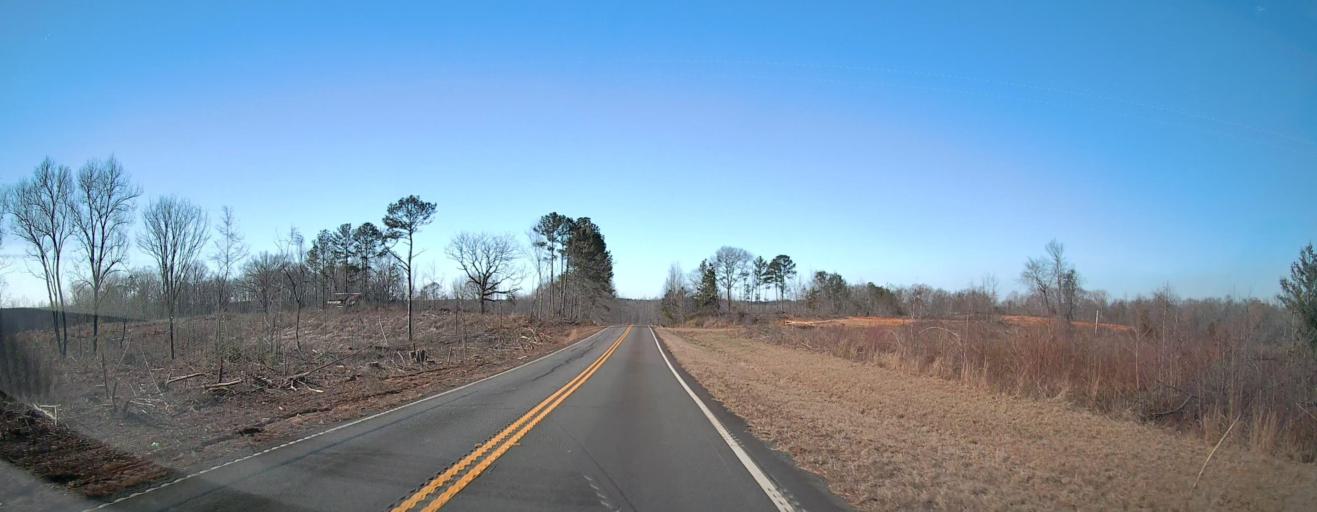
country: US
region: Georgia
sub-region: Talbot County
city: Talbotton
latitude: 32.6659
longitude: -84.4642
